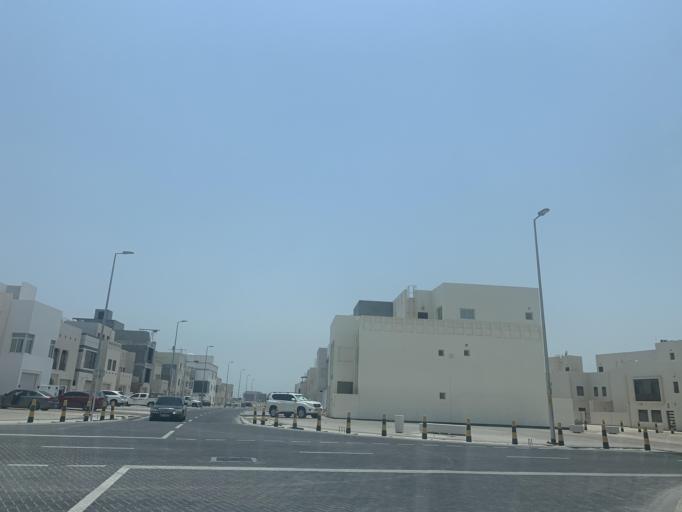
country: BH
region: Muharraq
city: Al Hadd
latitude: 26.2333
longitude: 50.6722
